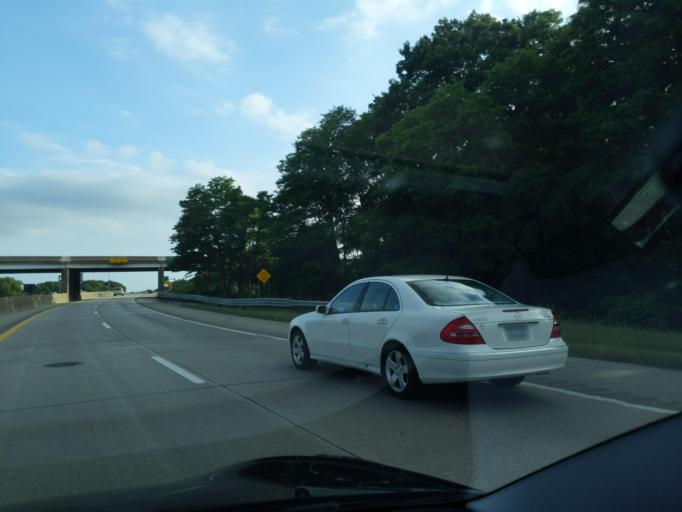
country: US
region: Michigan
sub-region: Muskegon County
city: Muskegon Heights
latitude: 43.1742
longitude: -86.2052
